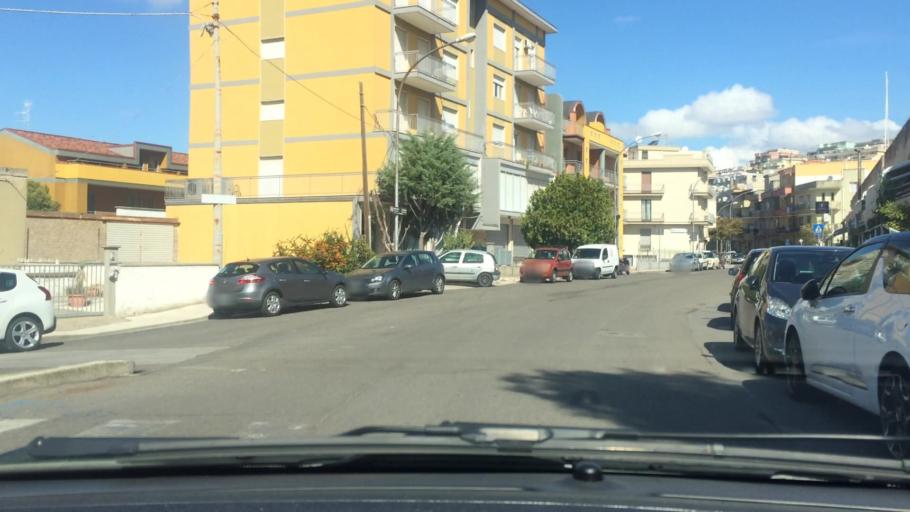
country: IT
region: Basilicate
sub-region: Provincia di Matera
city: Montescaglioso
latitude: 40.5458
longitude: 16.6670
